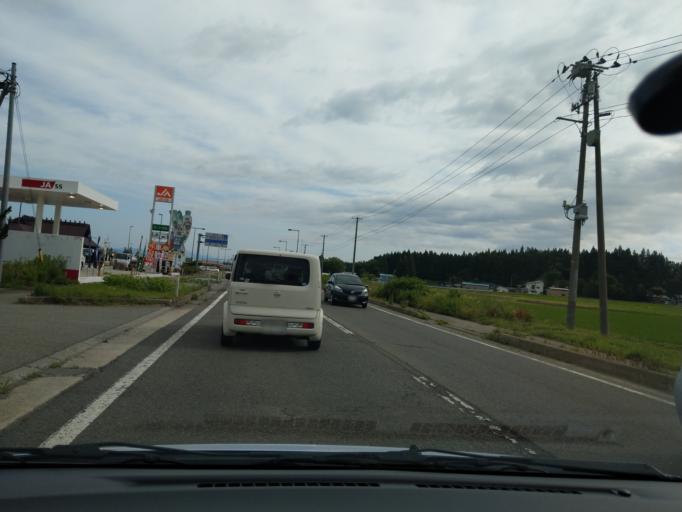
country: JP
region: Akita
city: Yokotemachi
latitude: 39.3780
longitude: 140.5682
